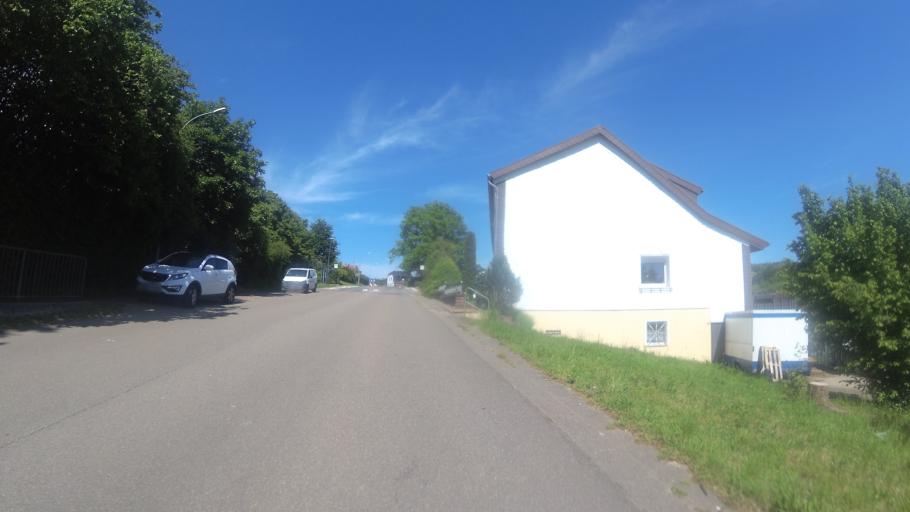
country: DE
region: Saarland
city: Quierschied
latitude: 49.3162
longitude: 7.0478
